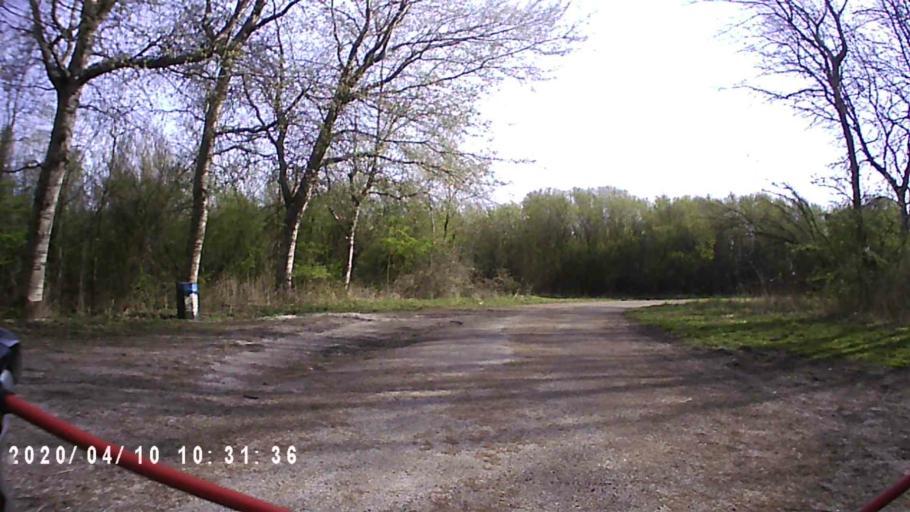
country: NL
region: Friesland
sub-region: Gemeente Dongeradeel
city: Anjum
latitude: 53.3931
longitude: 6.2119
